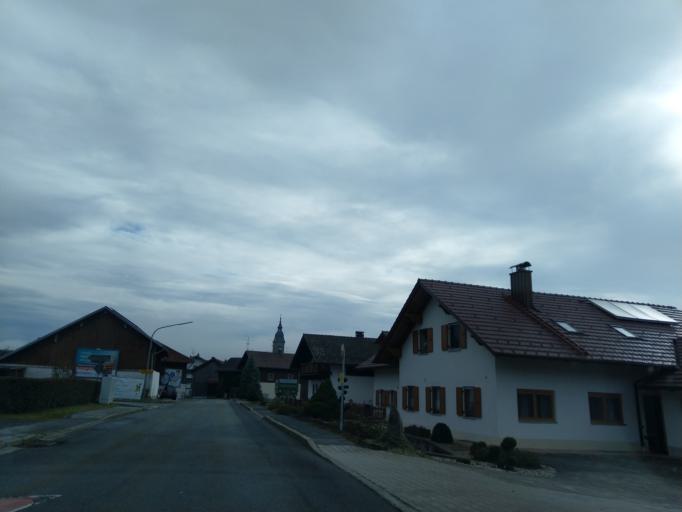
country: DE
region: Bavaria
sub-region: Lower Bavaria
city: Zenting
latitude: 48.7924
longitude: 13.2557
